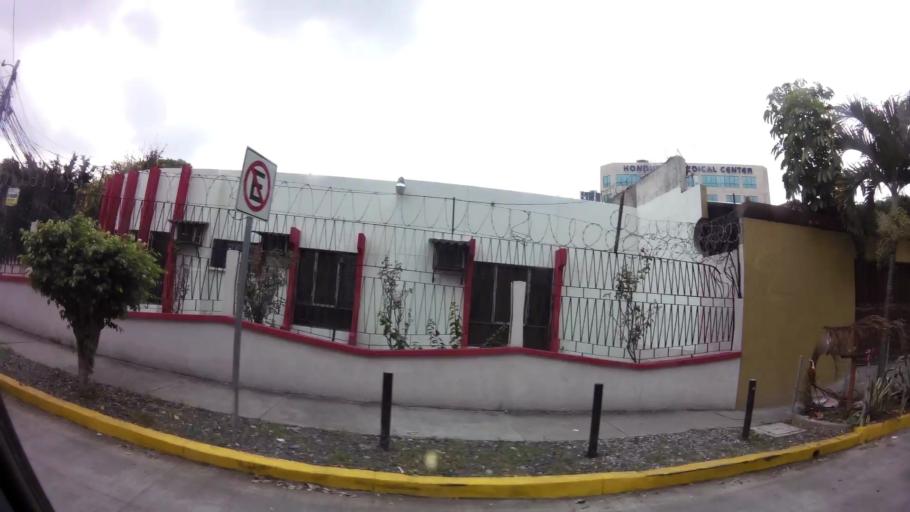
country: HN
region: Francisco Morazan
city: Tegucigalpa
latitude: 14.0965
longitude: -87.1908
